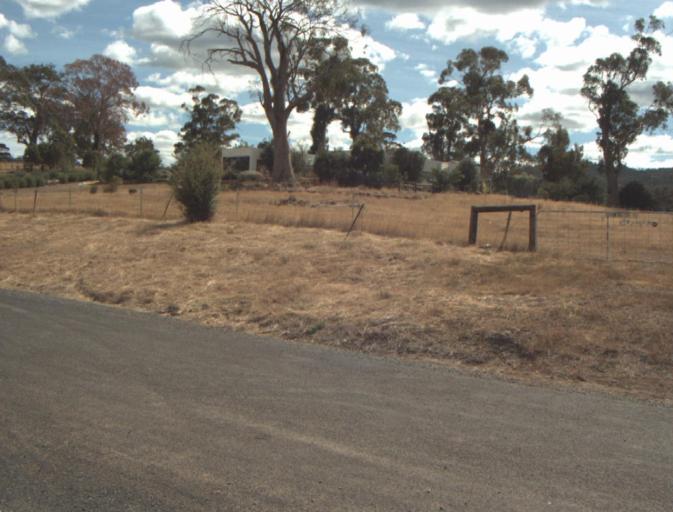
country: AU
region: Tasmania
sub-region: Launceston
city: Mayfield
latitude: -41.3467
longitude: 147.0878
